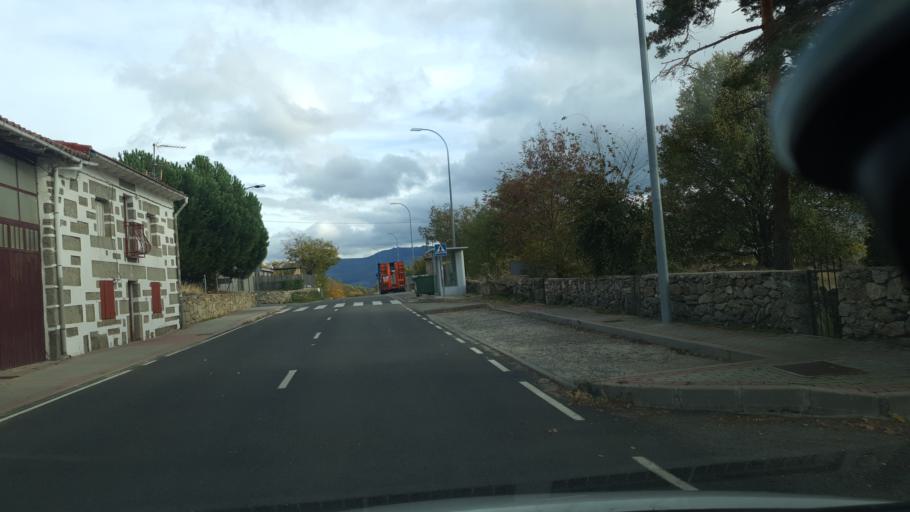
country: ES
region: Castille and Leon
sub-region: Provincia de Avila
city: Hoyocasero
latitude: 40.3979
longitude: -4.9760
